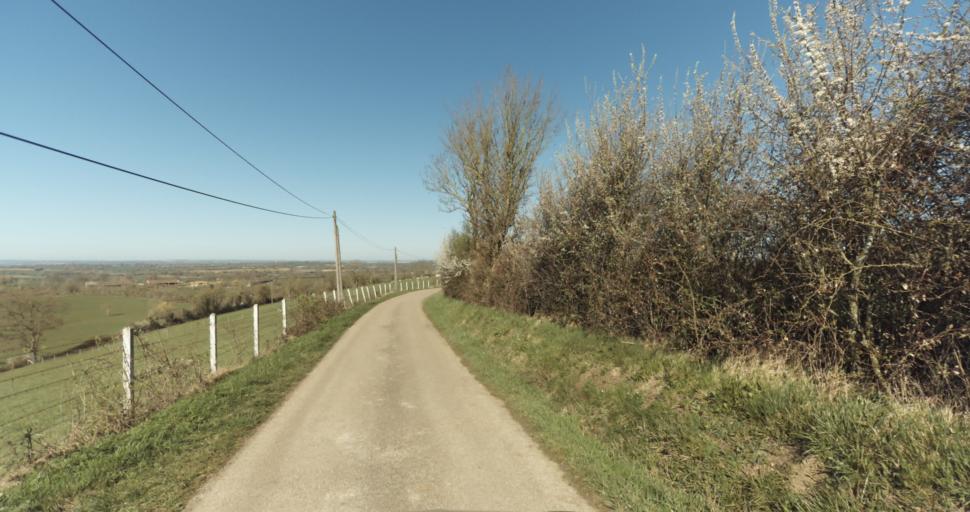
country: FR
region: Lower Normandy
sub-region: Departement de l'Orne
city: Trun
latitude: 48.9251
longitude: 0.0526
